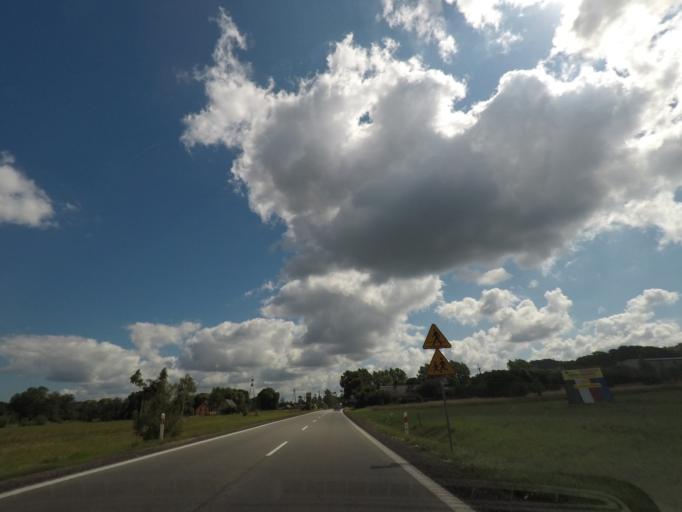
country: PL
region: Pomeranian Voivodeship
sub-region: Powiat wejherowski
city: Leczyce
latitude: 54.5754
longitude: 17.9025
